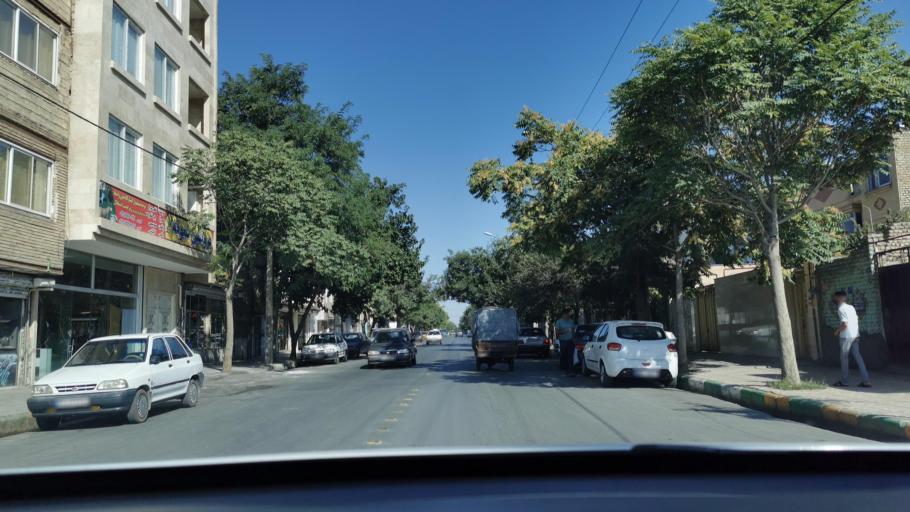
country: IR
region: Razavi Khorasan
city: Mashhad
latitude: 36.3350
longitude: 59.6381
